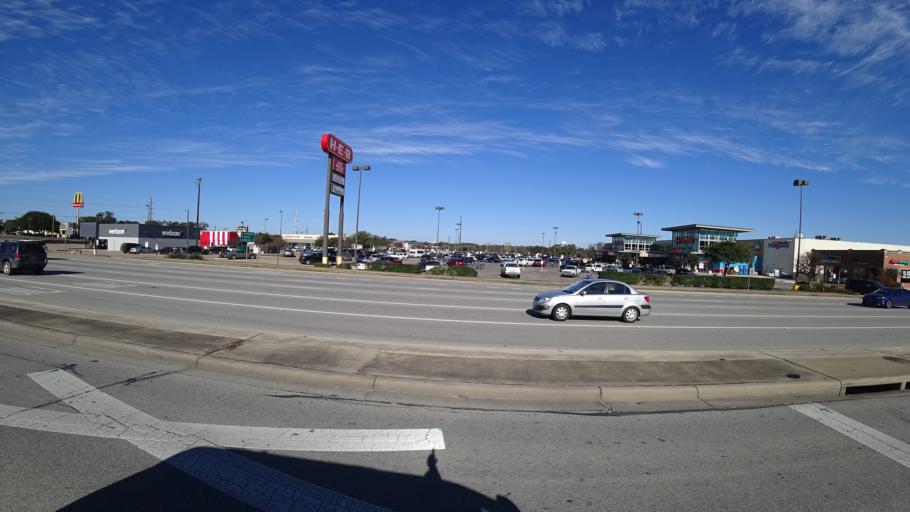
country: US
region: Texas
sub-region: Williamson County
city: Cedar Park
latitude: 30.5209
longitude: -97.8290
